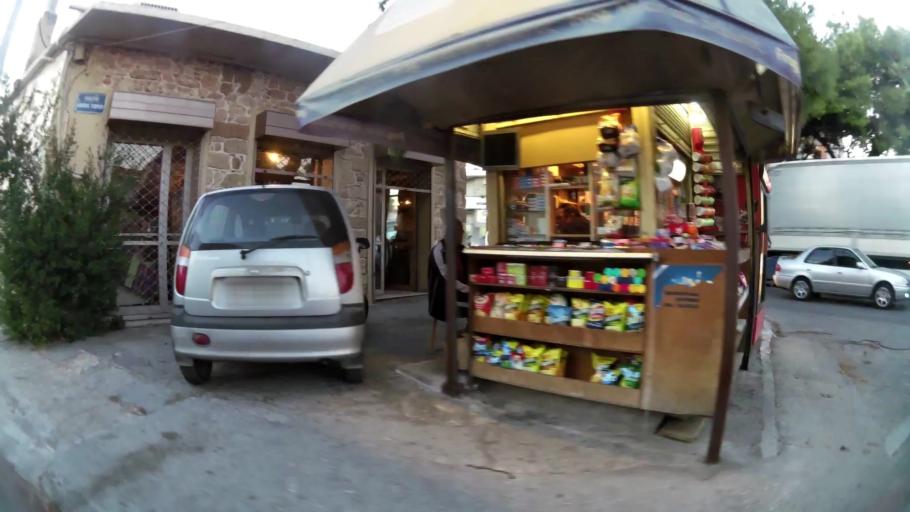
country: GR
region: Attica
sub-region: Nomarchia Anatolikis Attikis
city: Paiania
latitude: 37.9517
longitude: 23.8616
